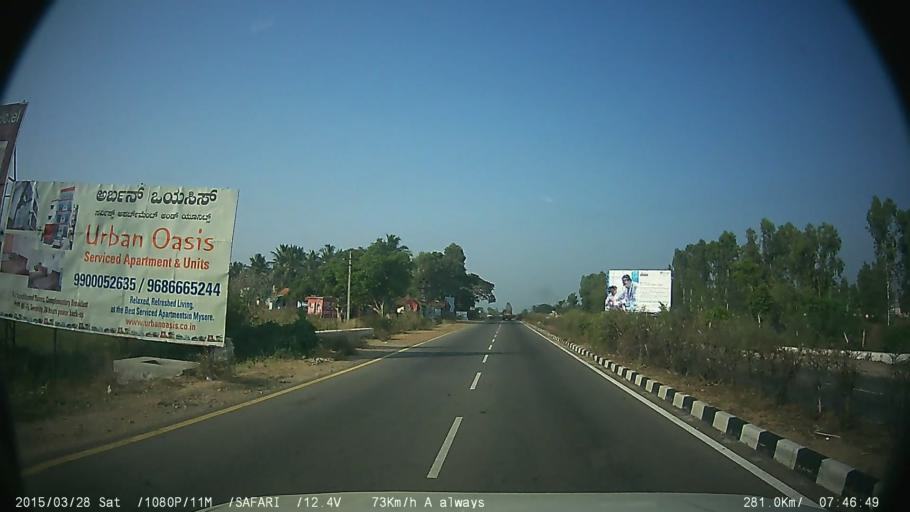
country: IN
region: Karnataka
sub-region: Mandya
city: Pandavapura
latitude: 12.4896
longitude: 76.7828
